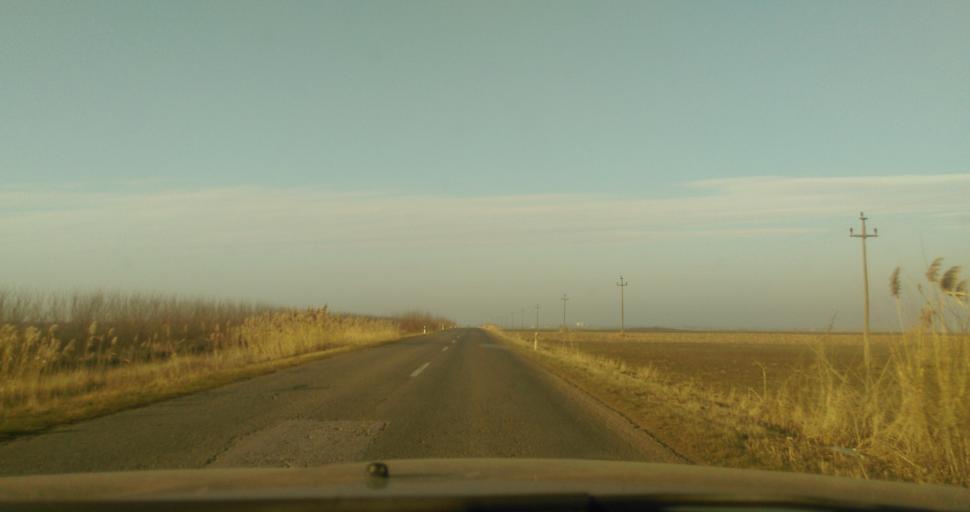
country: RS
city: Curug
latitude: 45.4906
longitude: 20.0361
